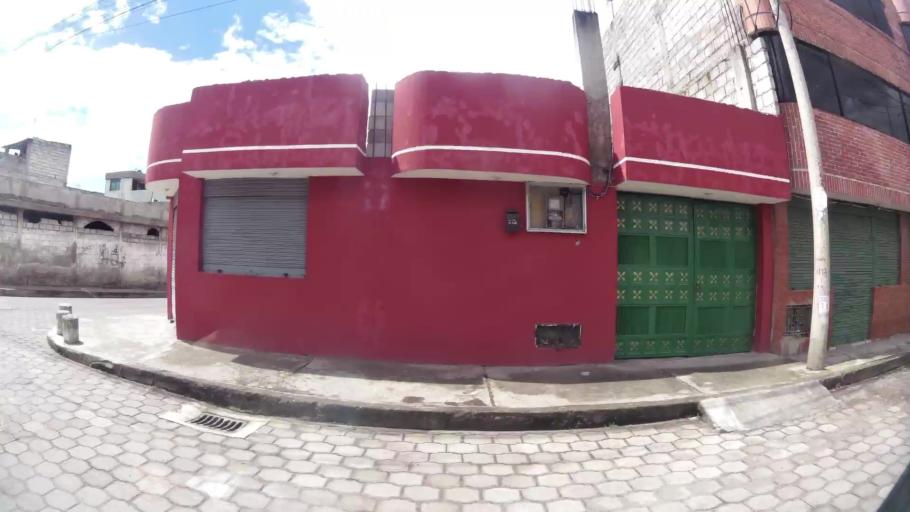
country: EC
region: Pichincha
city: Sangolqui
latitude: -0.3399
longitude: -78.5438
